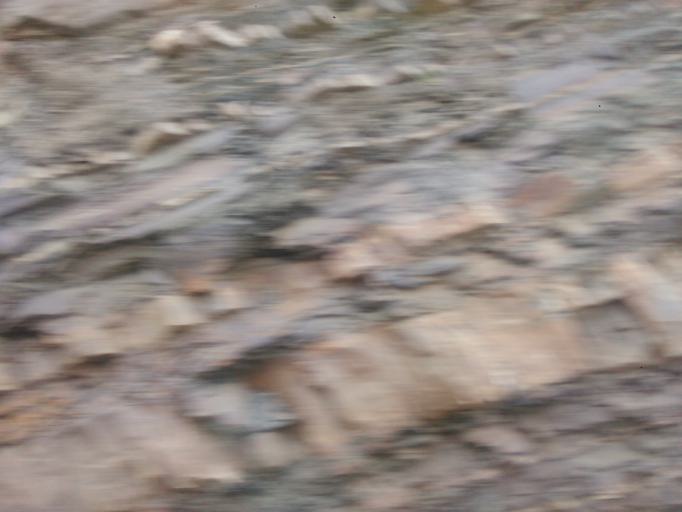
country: GE
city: Zhinvali
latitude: 42.1945
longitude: 44.8257
